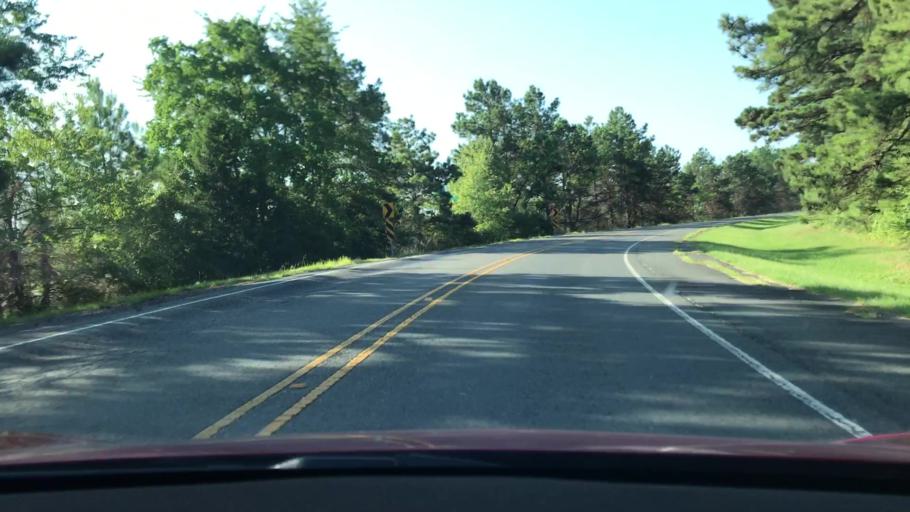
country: US
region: Louisiana
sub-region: Caddo Parish
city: Shreveport
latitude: 32.4530
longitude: -93.8443
